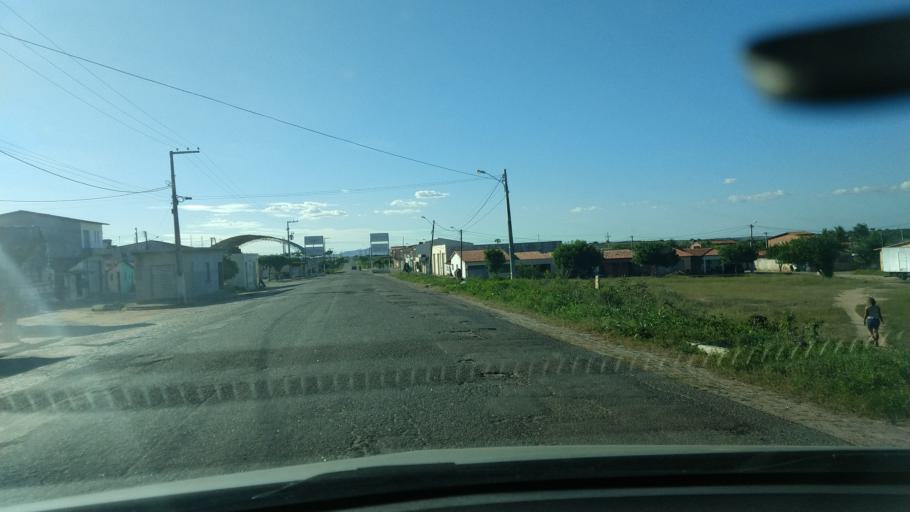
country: BR
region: Rio Grande do Norte
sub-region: Sao Jose Do Campestre
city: Sao Jose do Campestre
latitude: -6.4270
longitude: -35.6465
